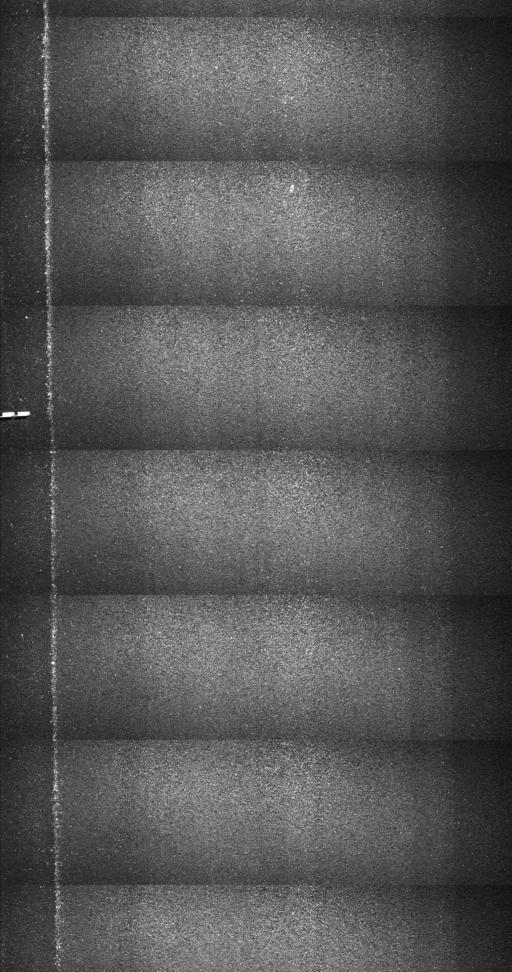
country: US
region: Vermont
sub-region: Franklin County
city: Richford
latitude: 44.8460
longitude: -72.6104
